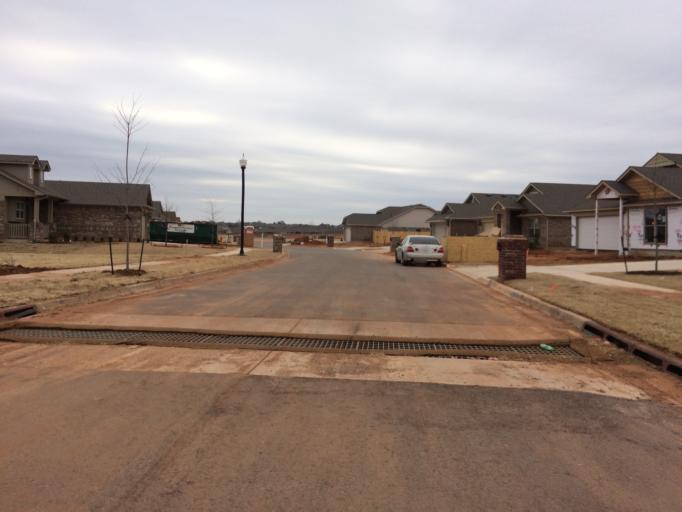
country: US
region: Oklahoma
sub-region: Cleveland County
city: Norman
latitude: 35.2572
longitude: -97.4575
